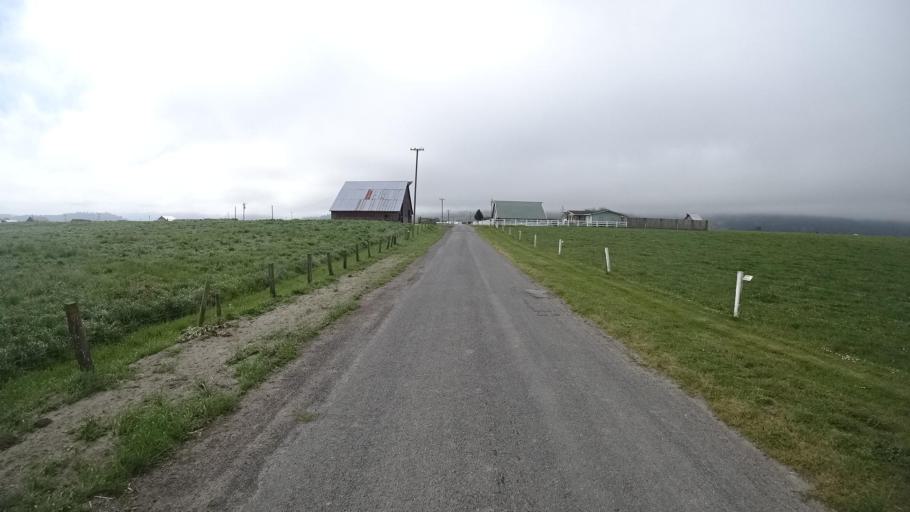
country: US
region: California
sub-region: Humboldt County
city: Fortuna
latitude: 40.5804
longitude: -124.1878
